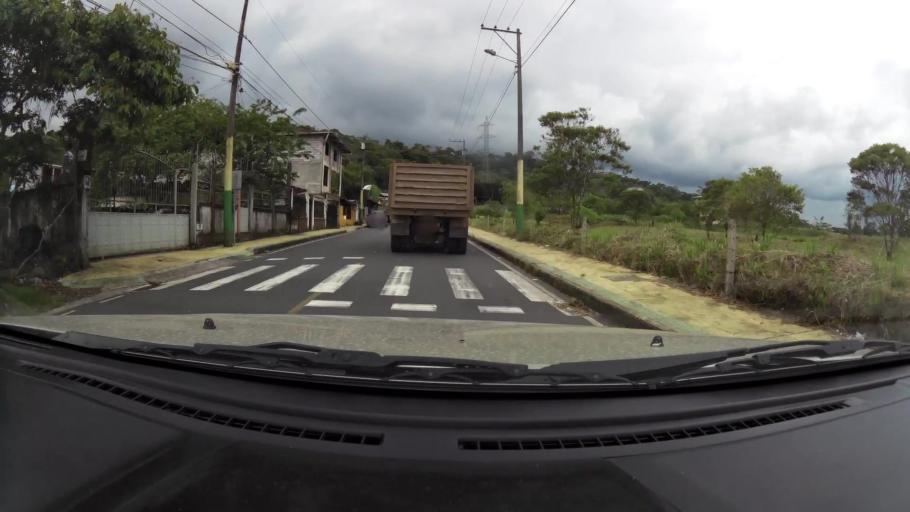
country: EC
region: Pastaza
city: Puyo
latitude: -1.4913
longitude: -78.0157
